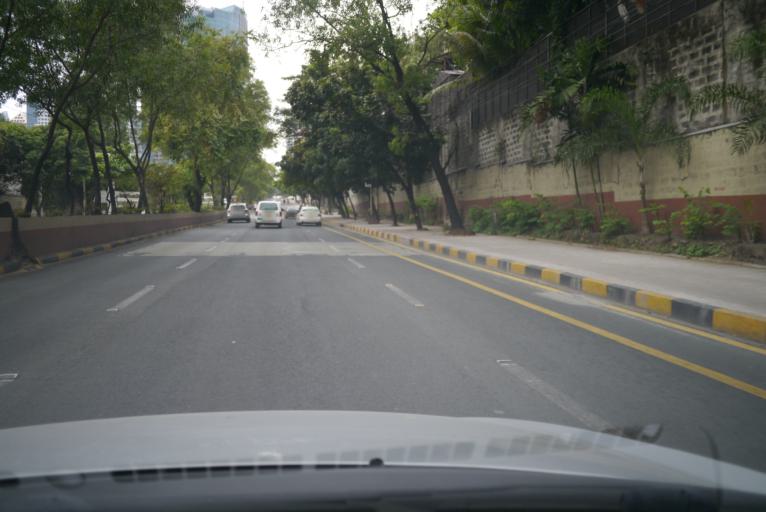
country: PH
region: Metro Manila
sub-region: Pasig
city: Pasig City
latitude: 14.5843
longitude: 121.0687
